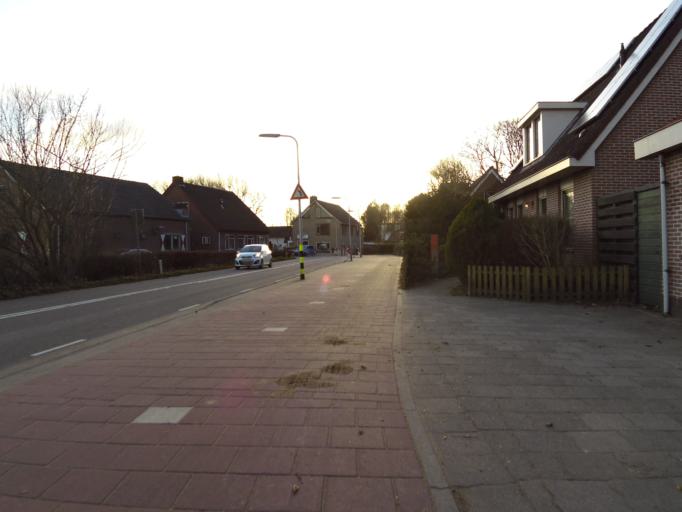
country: NL
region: South Holland
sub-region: Gemeente Noordwijkerhout
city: Noordwijkerhout
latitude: 52.2705
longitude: 4.4676
